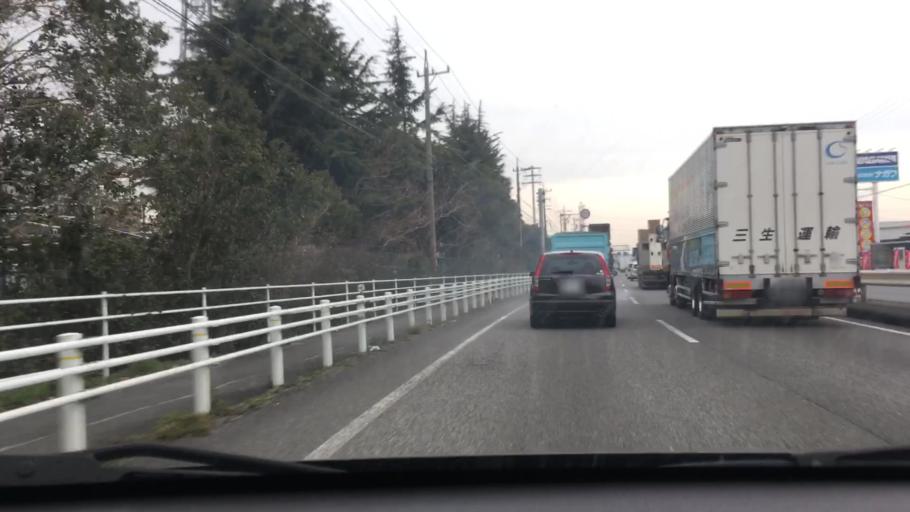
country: JP
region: Mie
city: Yokkaichi
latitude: 34.9362
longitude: 136.6154
